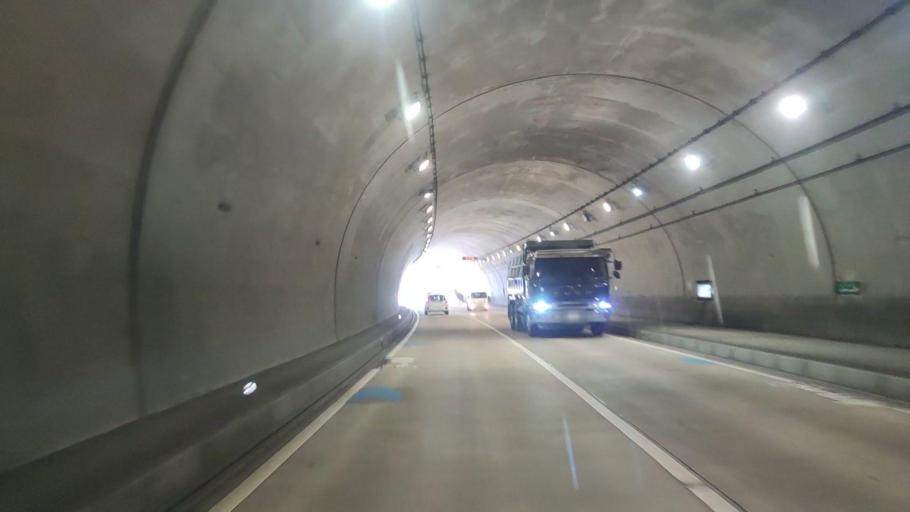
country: JP
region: Wakayama
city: Shingu
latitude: 33.7372
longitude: 135.9889
